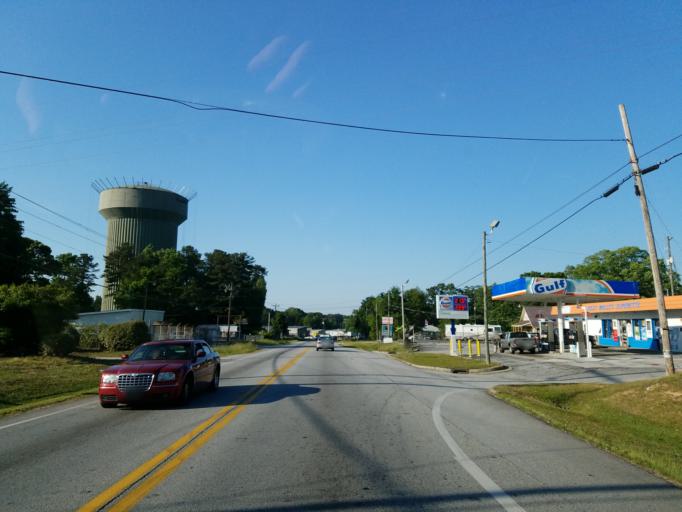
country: US
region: Georgia
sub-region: Douglas County
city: Lithia Springs
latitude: 33.7817
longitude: -84.7031
